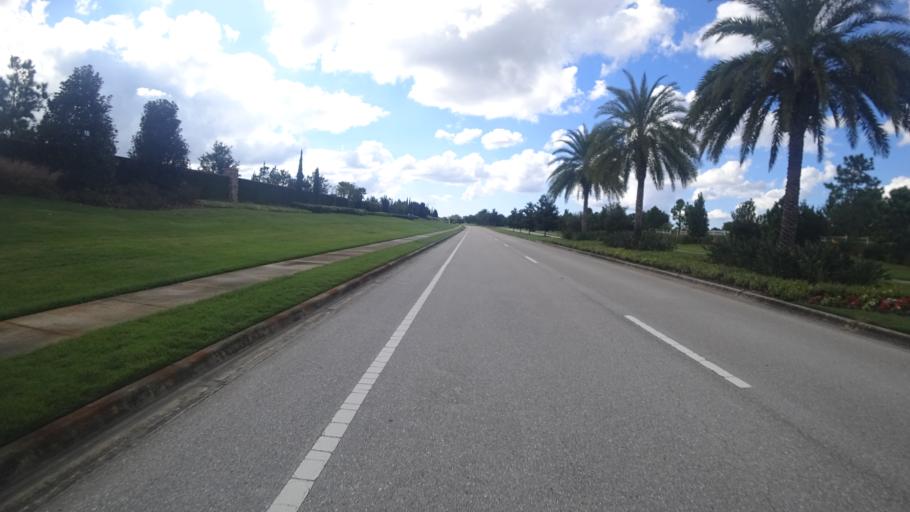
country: US
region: Florida
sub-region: Sarasota County
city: The Meadows
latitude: 27.4020
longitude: -82.3787
